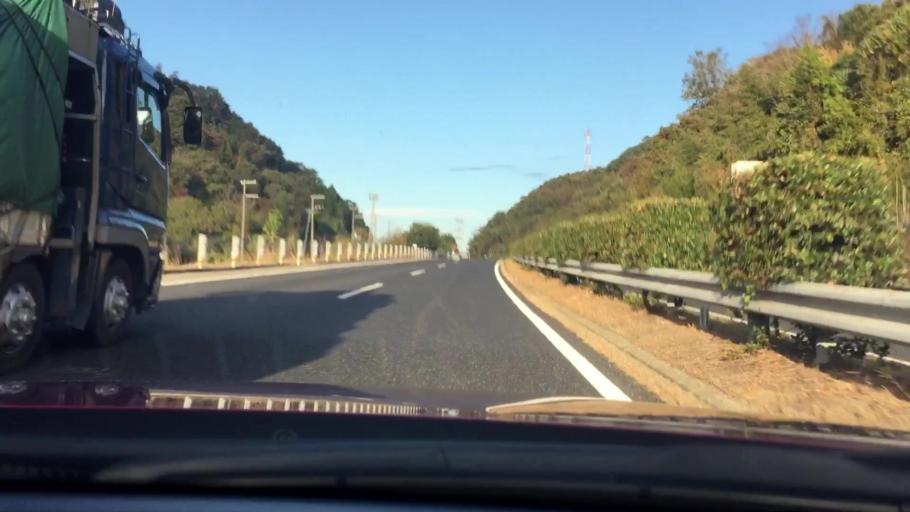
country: JP
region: Hyogo
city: Yamazakicho-nakabirose
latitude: 34.9793
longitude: 134.6249
